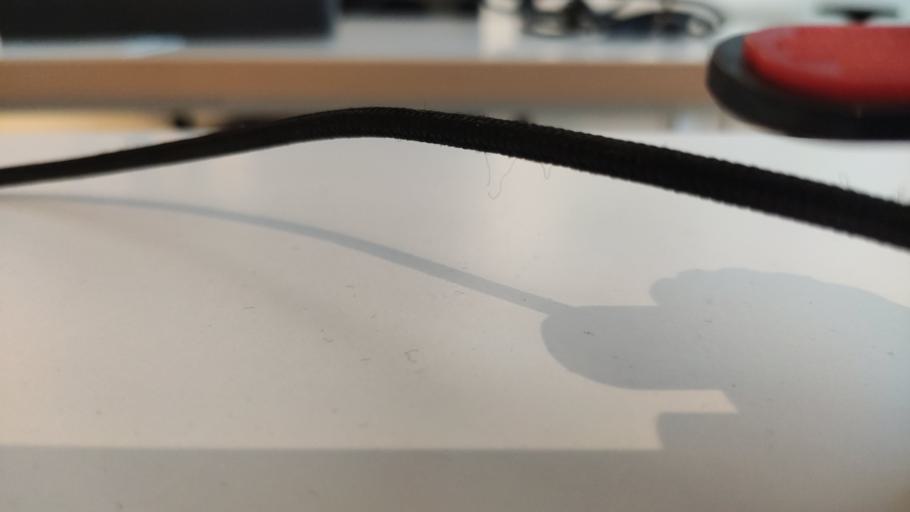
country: RU
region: Moskovskaya
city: Novopetrovskoye
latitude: 55.9760
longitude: 36.4446
